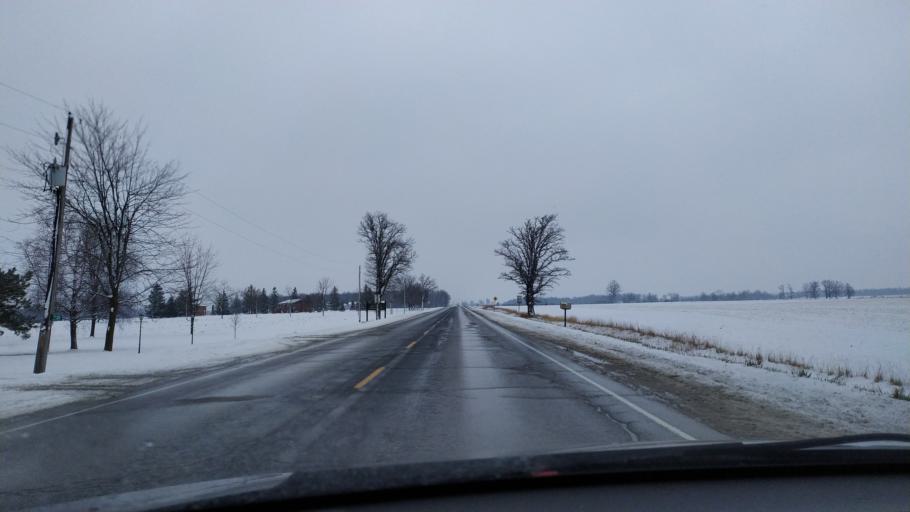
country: CA
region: Ontario
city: North Perth
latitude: 43.5817
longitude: -80.8320
